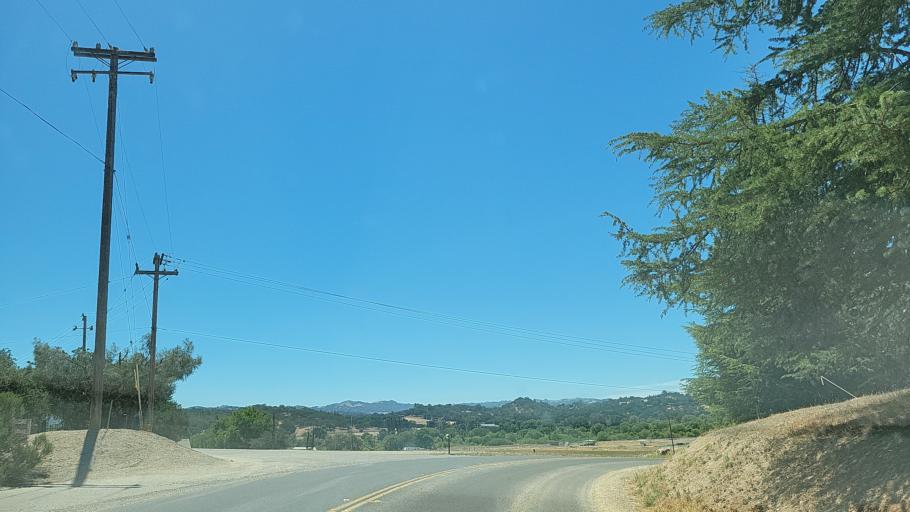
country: US
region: California
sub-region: San Luis Obispo County
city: Atascadero
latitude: 35.4807
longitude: -120.6295
